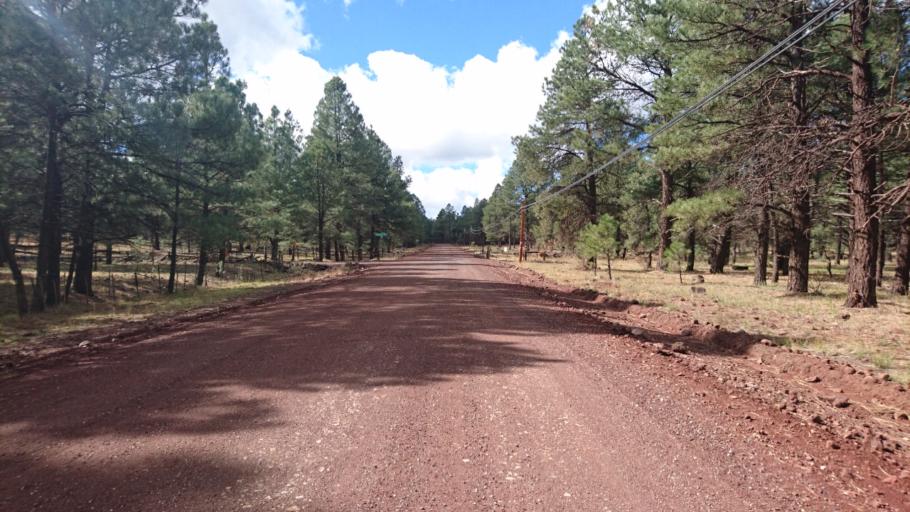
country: US
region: Arizona
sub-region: Coconino County
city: Williams
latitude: 35.2650
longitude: -112.0837
